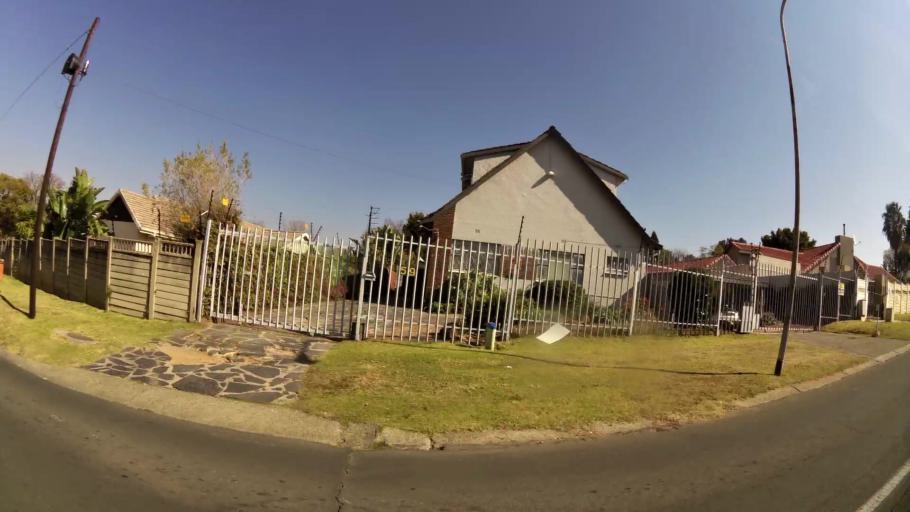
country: ZA
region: Gauteng
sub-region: City of Johannesburg Metropolitan Municipality
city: Johannesburg
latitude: -26.1440
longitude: 28.1023
